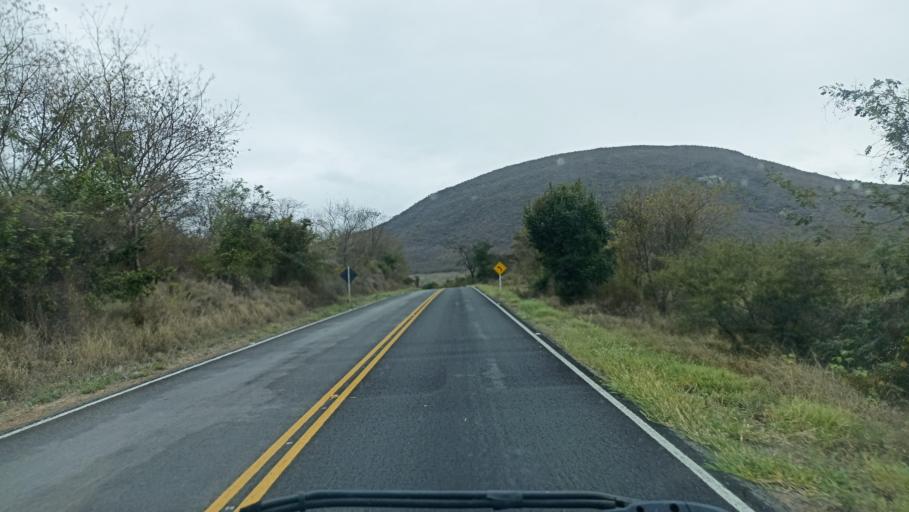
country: BR
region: Bahia
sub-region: Andarai
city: Vera Cruz
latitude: -13.0487
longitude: -40.7817
